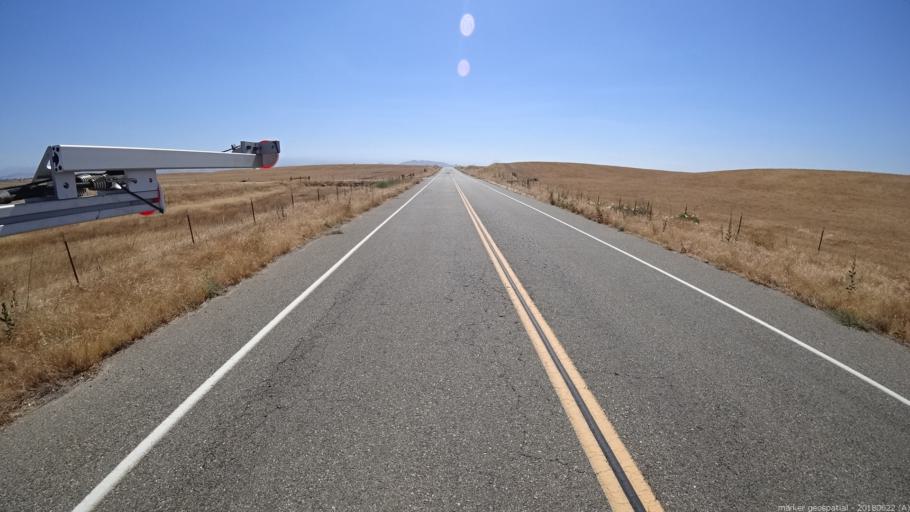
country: US
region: California
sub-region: Madera County
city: Bonadelle Ranchos-Madera Ranchos
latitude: 36.9232
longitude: -119.7811
